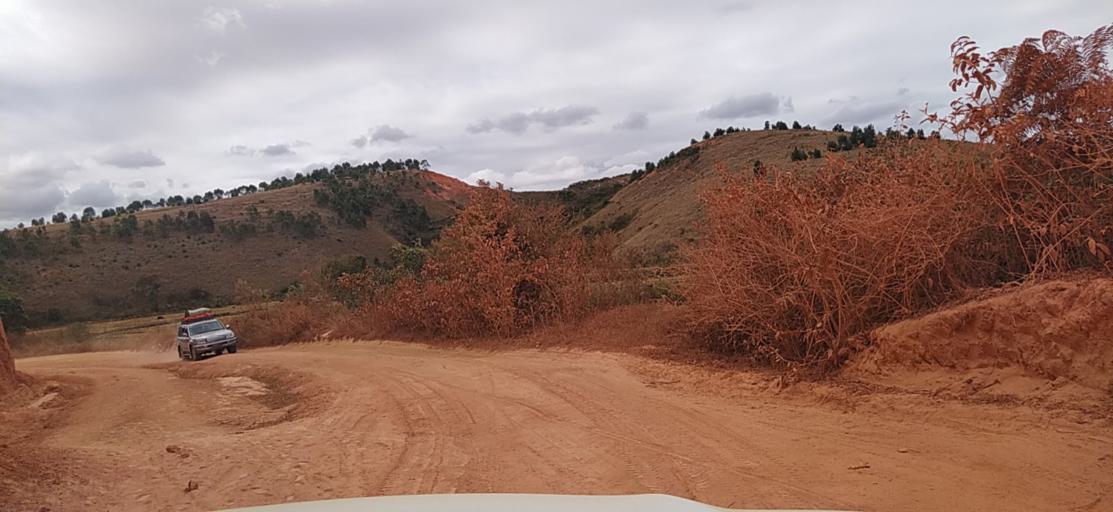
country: MG
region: Alaotra Mangoro
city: Ambatondrazaka
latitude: -18.0046
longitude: 48.2632
